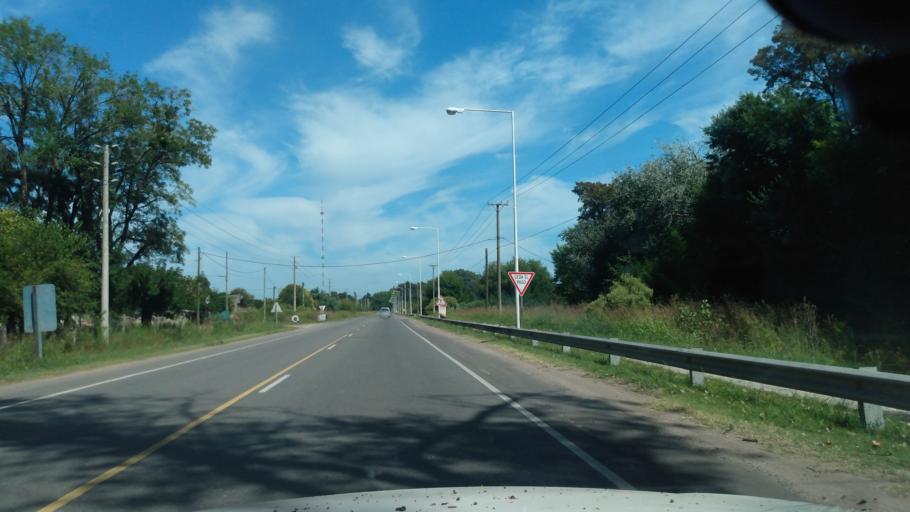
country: AR
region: Buenos Aires
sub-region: Partido de Lujan
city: Lujan
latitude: -34.5491
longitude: -59.1412
